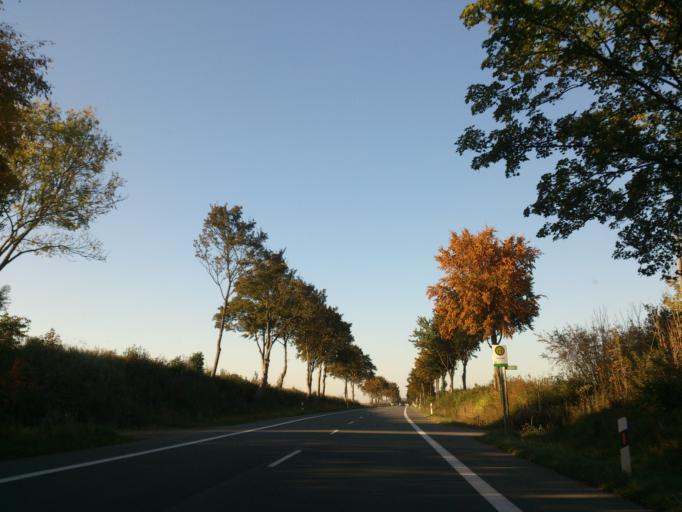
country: DE
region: North Rhine-Westphalia
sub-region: Regierungsbezirk Detmold
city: Willebadessen
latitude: 51.5946
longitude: 9.0336
